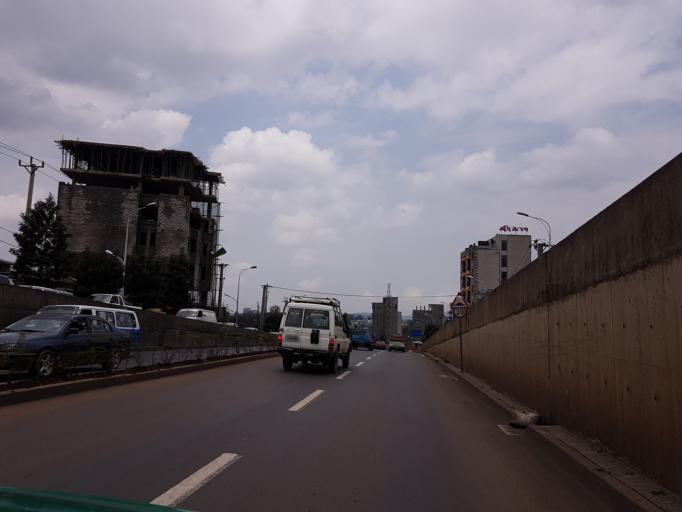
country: ET
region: Adis Abeba
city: Addis Ababa
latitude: 9.0102
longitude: 38.7340
